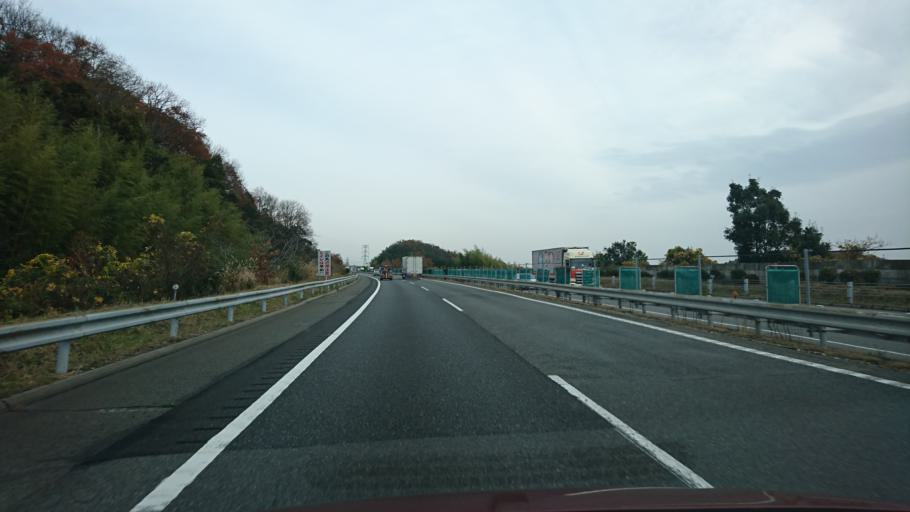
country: JP
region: Hyogo
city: Sandacho
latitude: 34.8232
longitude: 135.1450
